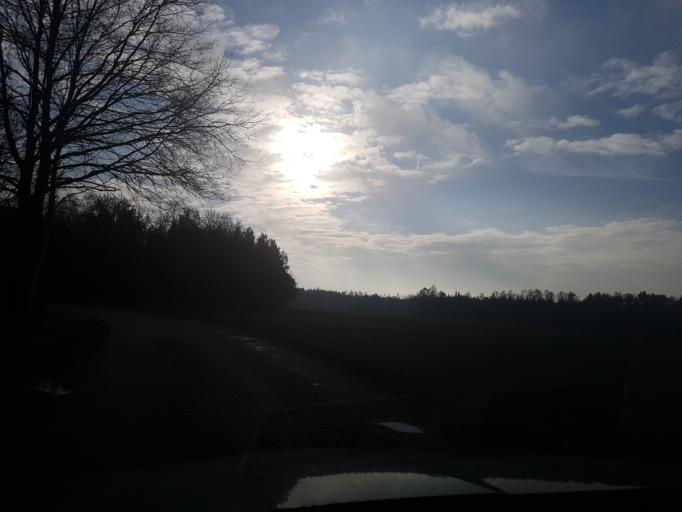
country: DE
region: Brandenburg
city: Ruckersdorf
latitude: 51.5482
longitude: 13.5981
